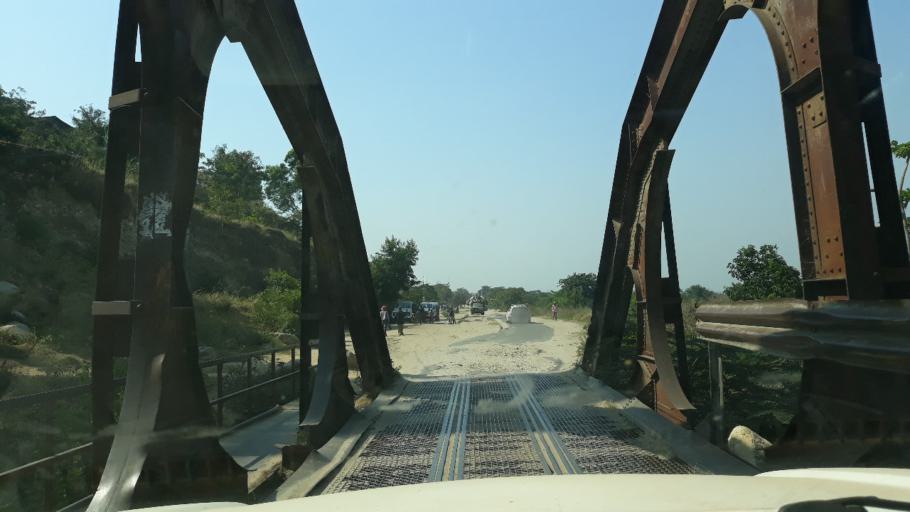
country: CD
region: South Kivu
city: Uvira
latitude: -3.2409
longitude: 29.1609
